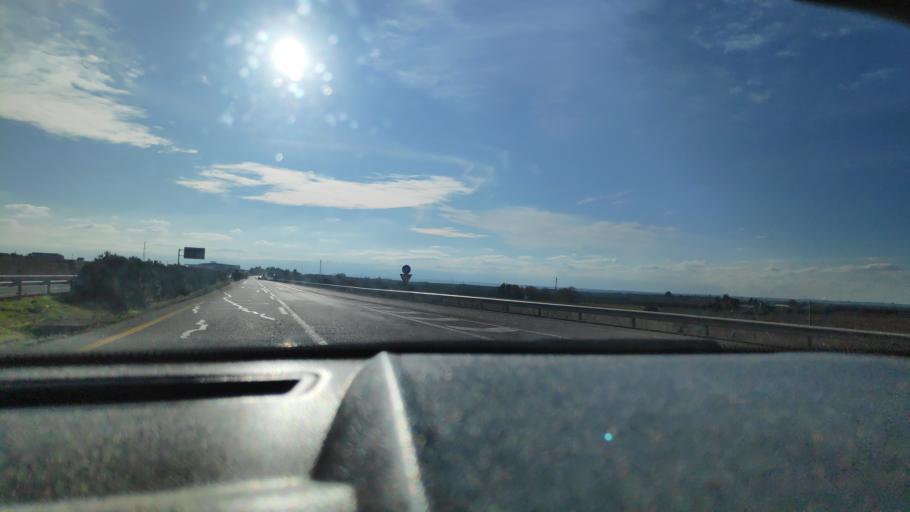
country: ES
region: Andalusia
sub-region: Provincia de Sevilla
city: Ecija
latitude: 37.5853
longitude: -4.9892
